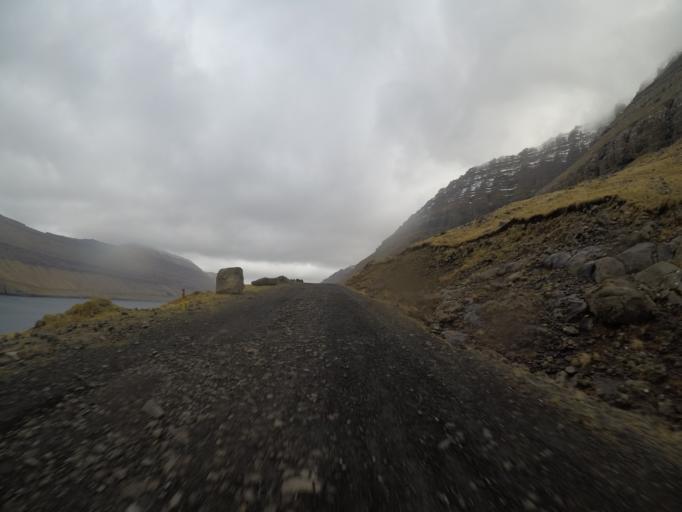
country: FO
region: Nordoyar
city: Klaksvik
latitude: 62.3388
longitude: -6.5796
